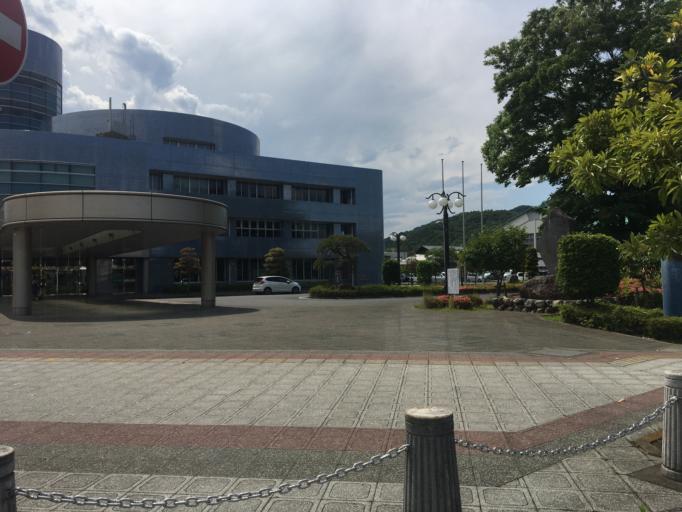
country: JP
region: Saitama
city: Yorii
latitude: 36.1185
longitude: 139.1938
